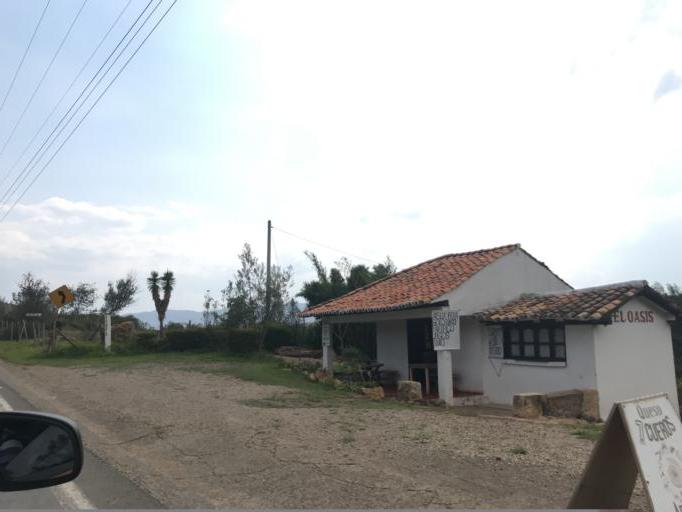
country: CO
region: Boyaca
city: Sachica
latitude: 5.6177
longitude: -73.5343
